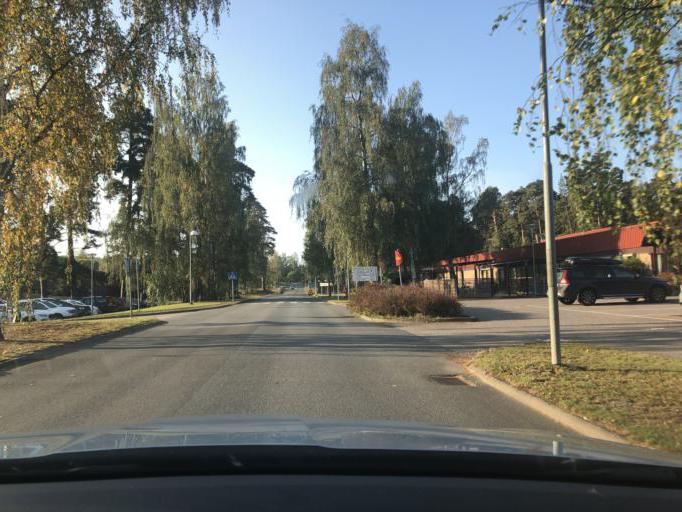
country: SE
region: Joenkoeping
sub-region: Jonkopings Kommun
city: Jonkoping
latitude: 57.7678
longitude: 14.1928
